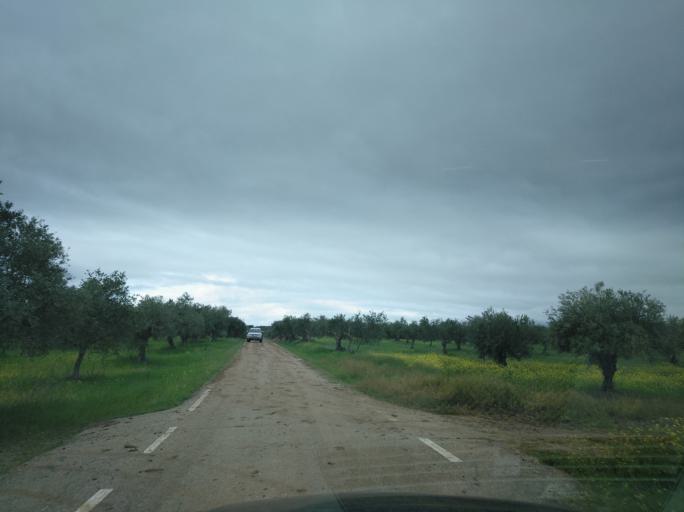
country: PT
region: Portalegre
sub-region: Campo Maior
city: Campo Maior
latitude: 38.9805
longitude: -7.0325
